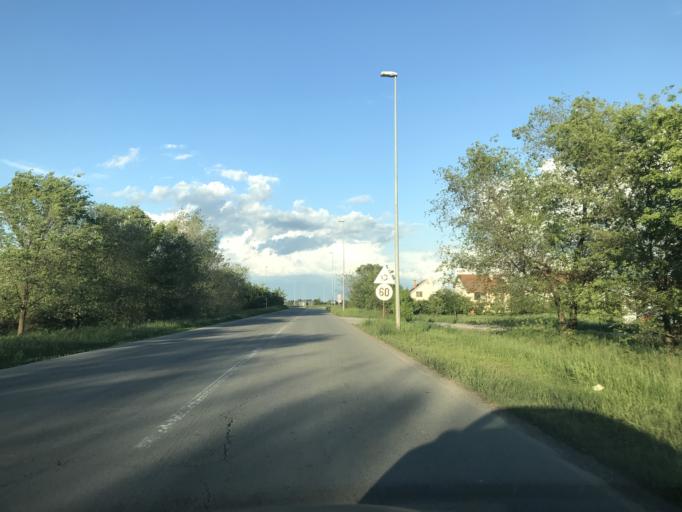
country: RS
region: Autonomna Pokrajina Vojvodina
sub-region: Srednjebanatski Okrug
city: Zrenjanin
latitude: 45.4014
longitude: 20.3744
